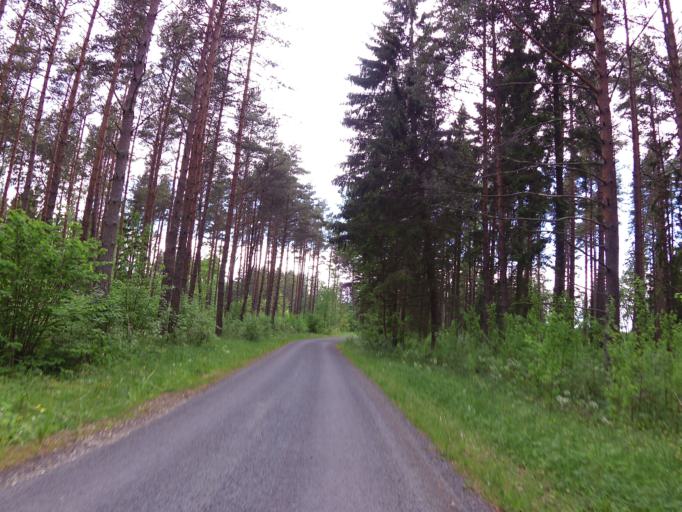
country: EE
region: Harju
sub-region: Paldiski linn
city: Paldiski
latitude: 59.2525
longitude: 23.7596
